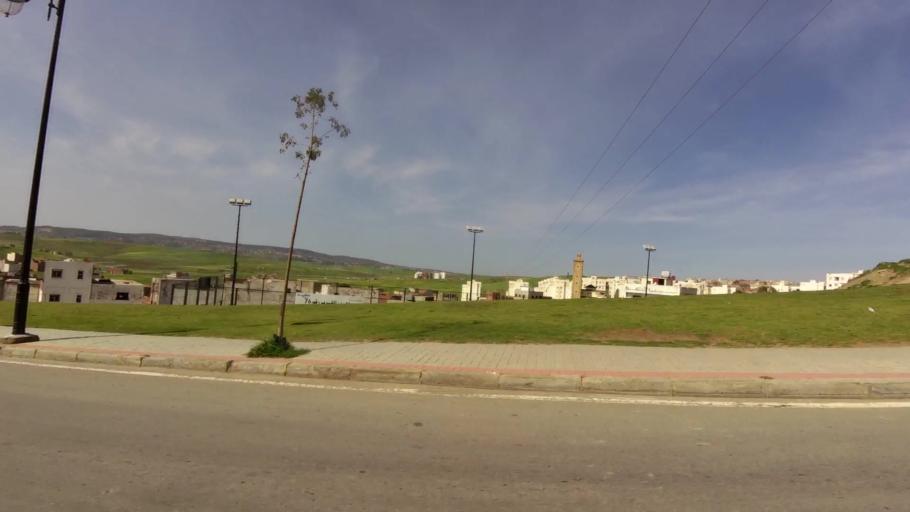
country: MA
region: Tanger-Tetouan
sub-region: Tanger-Assilah
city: Tangier
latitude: 35.7297
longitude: -5.8139
